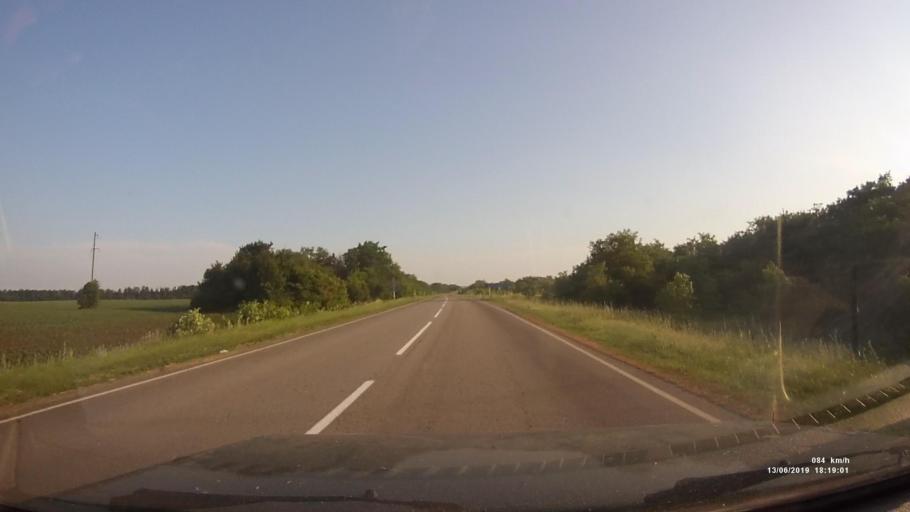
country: RU
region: Rostov
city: Kazanskaya
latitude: 49.9013
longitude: 41.3091
